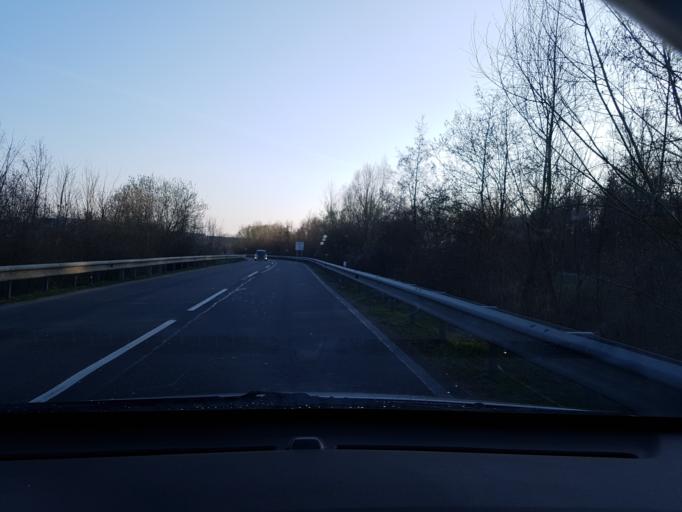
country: AT
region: Upper Austria
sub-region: Politischer Bezirk Linz-Land
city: Traun
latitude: 48.1798
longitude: 14.2488
